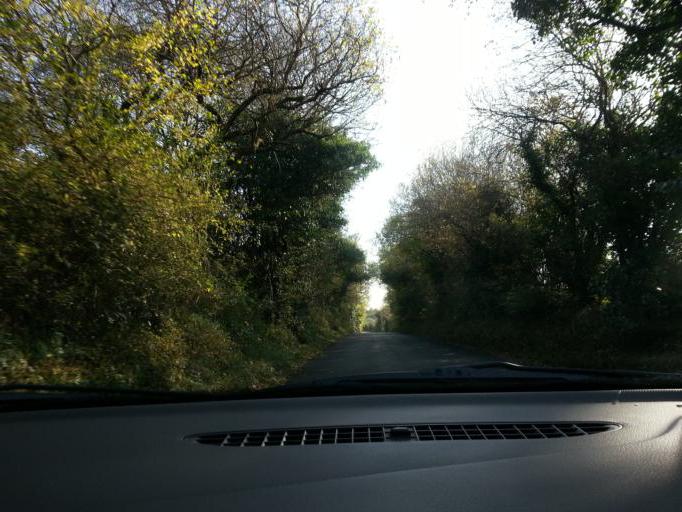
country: GB
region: Northern Ireland
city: Lisnaskea
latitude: 54.2427
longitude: -7.3773
